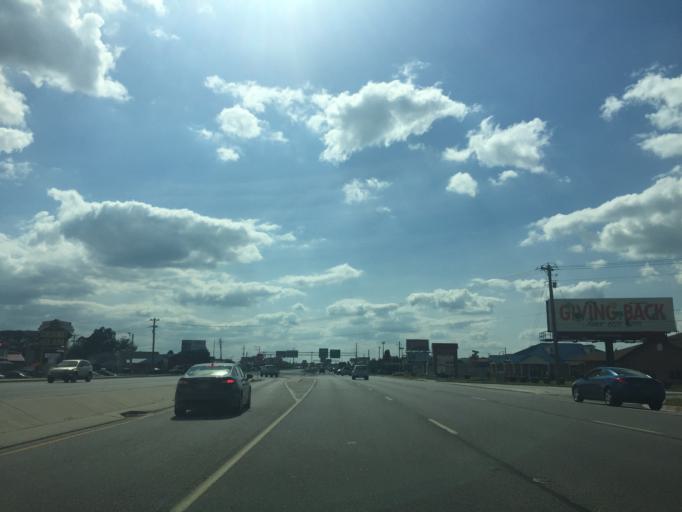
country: US
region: Delaware
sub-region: Sussex County
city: Lewes
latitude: 38.7486
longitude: -75.1641
